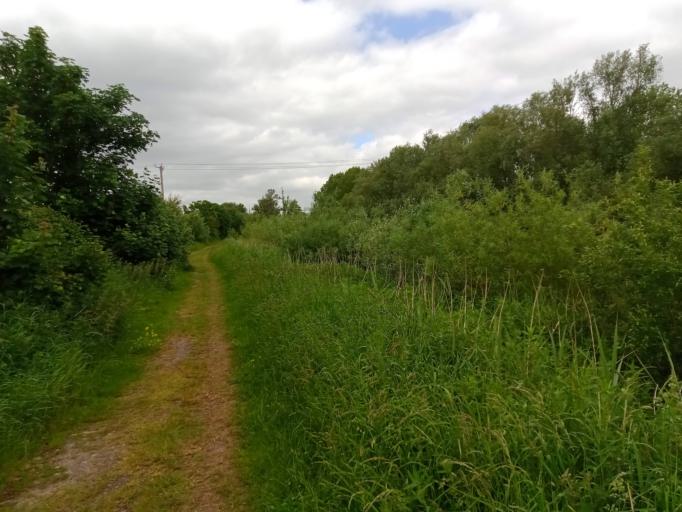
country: IE
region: Leinster
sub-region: County Carlow
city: Carlow
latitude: 52.8273
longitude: -6.9386
